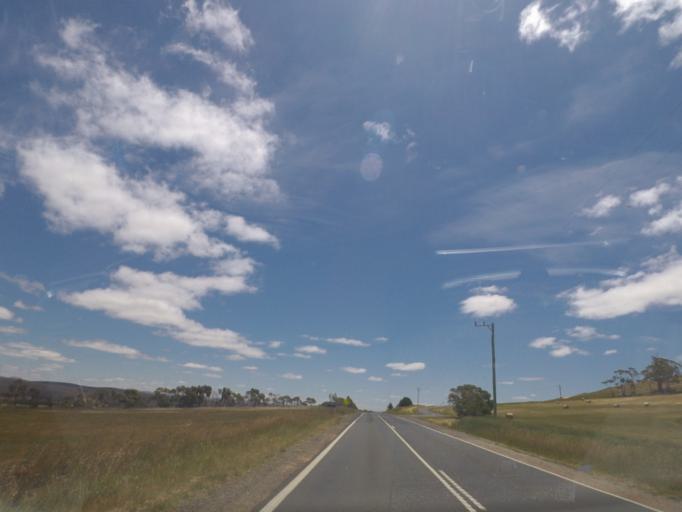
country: AU
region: Victoria
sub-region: Mount Alexander
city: Castlemaine
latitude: -37.2692
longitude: 144.1414
